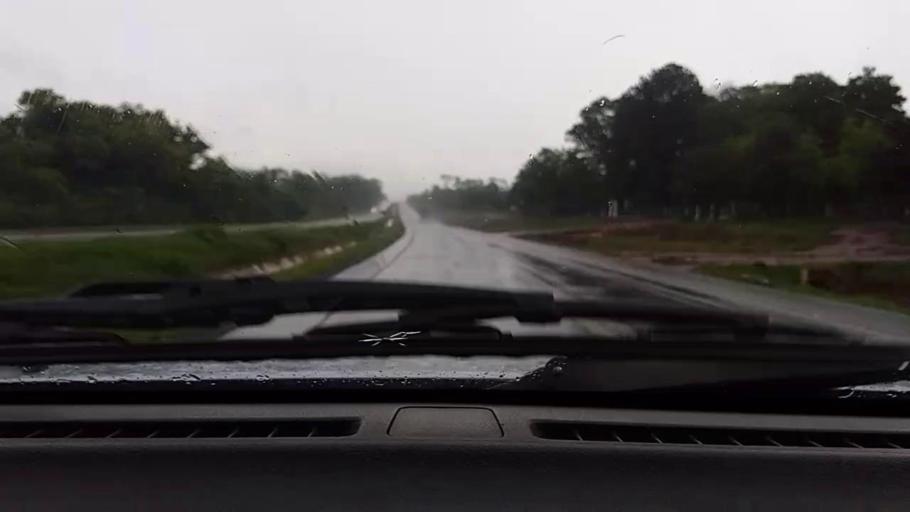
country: PY
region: Caaguazu
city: Repatriacion
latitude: -25.4481
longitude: -55.8936
